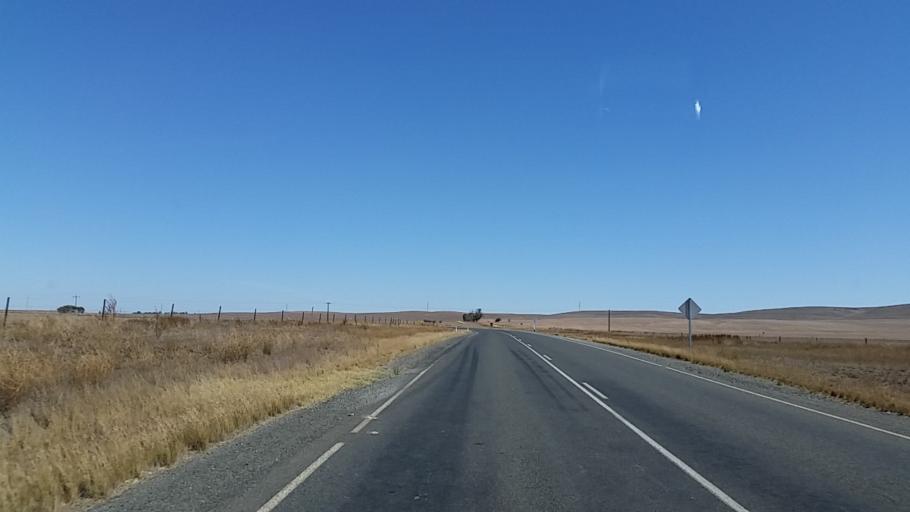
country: AU
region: South Australia
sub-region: Clare and Gilbert Valleys
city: Clare
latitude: -33.6823
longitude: 138.9085
